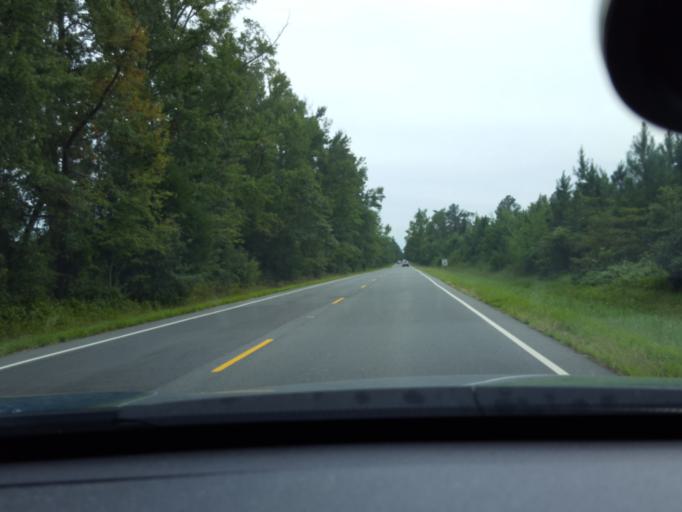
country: US
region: Virginia
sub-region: Caroline County
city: Bowling Green
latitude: 37.9871
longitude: -77.3381
